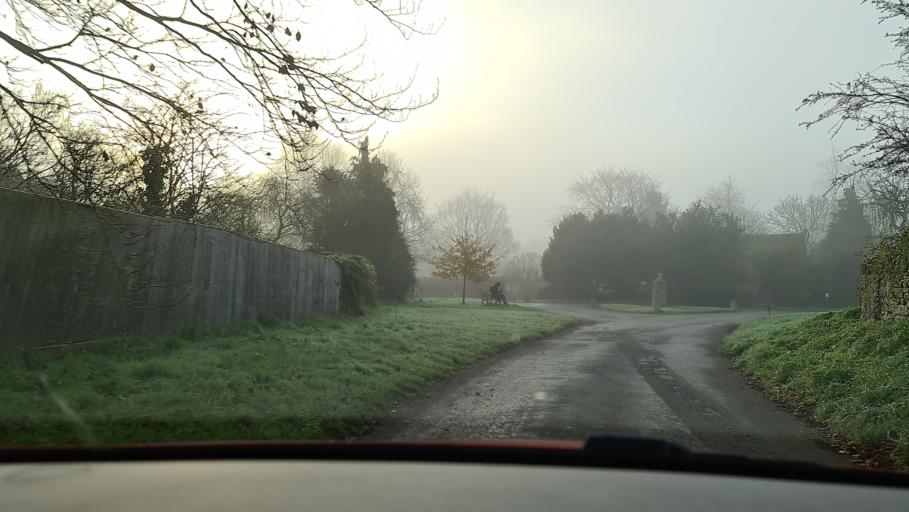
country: GB
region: England
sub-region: Buckinghamshire
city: Haddenham
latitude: 51.8043
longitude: -0.9383
